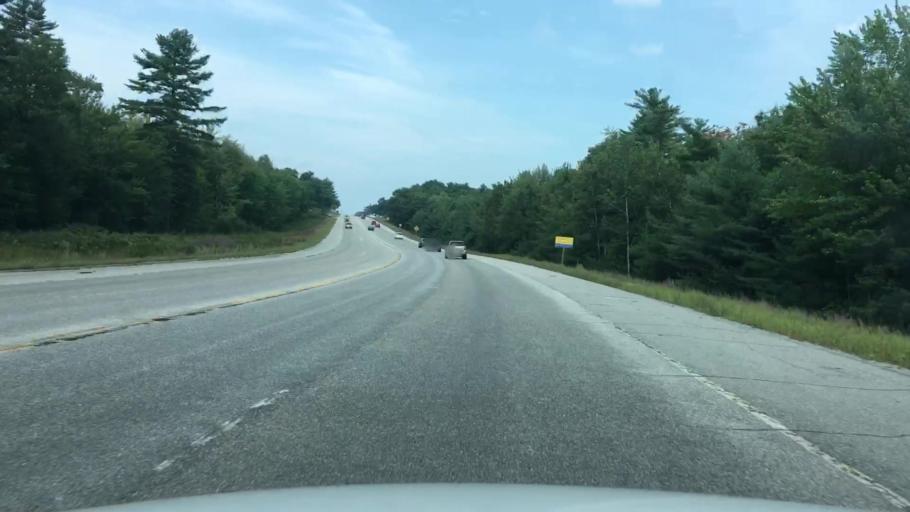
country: US
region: Maine
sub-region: Androscoggin County
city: Lewiston
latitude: 44.1790
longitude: -70.2318
